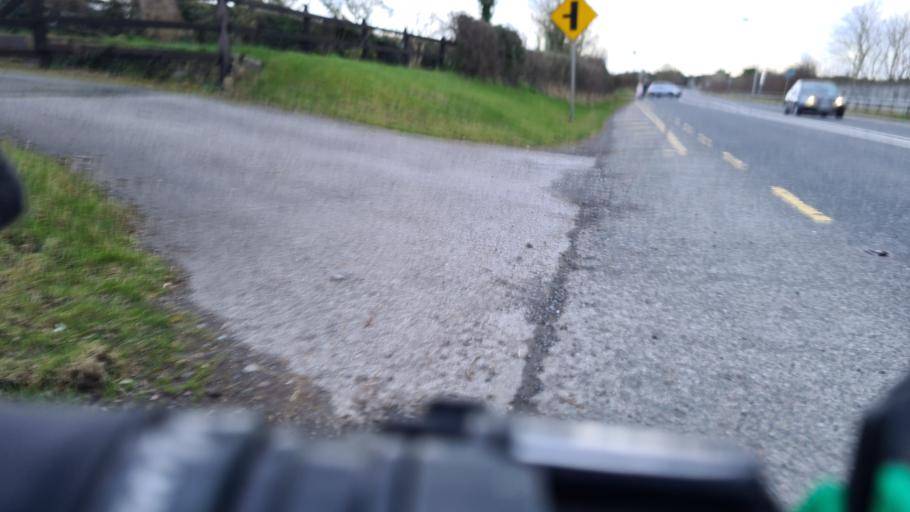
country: IE
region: Leinster
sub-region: Kildare
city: Maynooth
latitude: 53.3412
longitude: -6.6026
